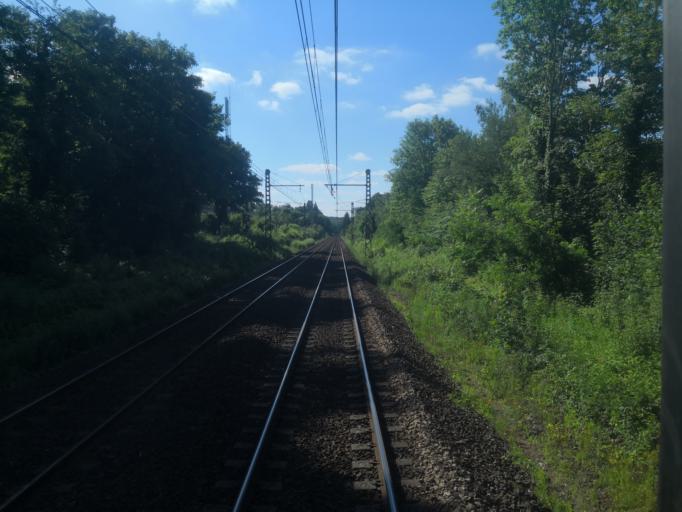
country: FR
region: Ile-de-France
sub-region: Departement de Seine-et-Marne
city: Chartrettes
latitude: 48.4781
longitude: 2.6877
